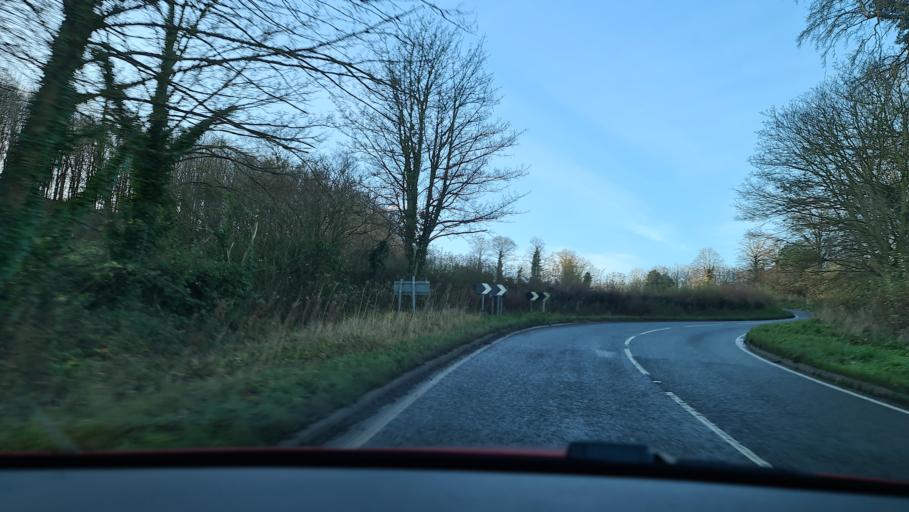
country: GB
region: England
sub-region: Buckinghamshire
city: Waddesdon
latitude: 51.8354
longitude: -0.9040
